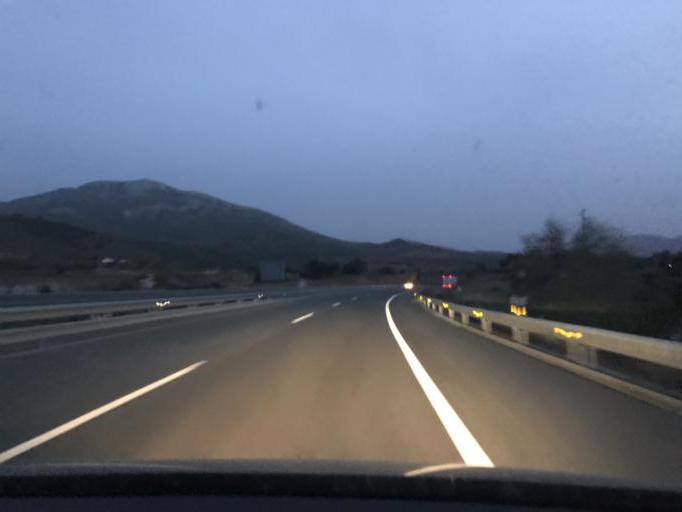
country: ES
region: Andalusia
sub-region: Provincia de Granada
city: Gor
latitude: 37.4108
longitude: -2.9188
